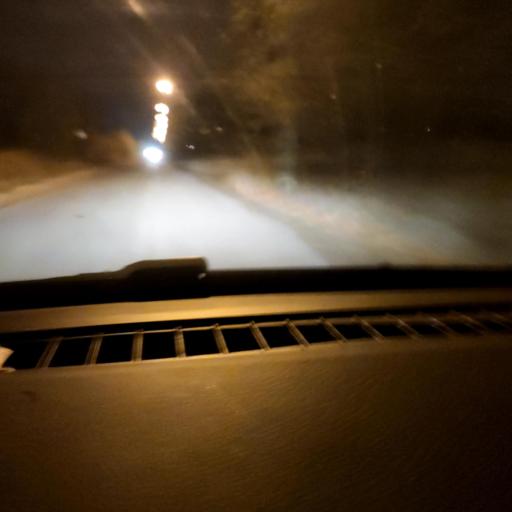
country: RU
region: Voronezj
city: Pridonskoy
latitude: 51.6848
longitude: 39.0918
